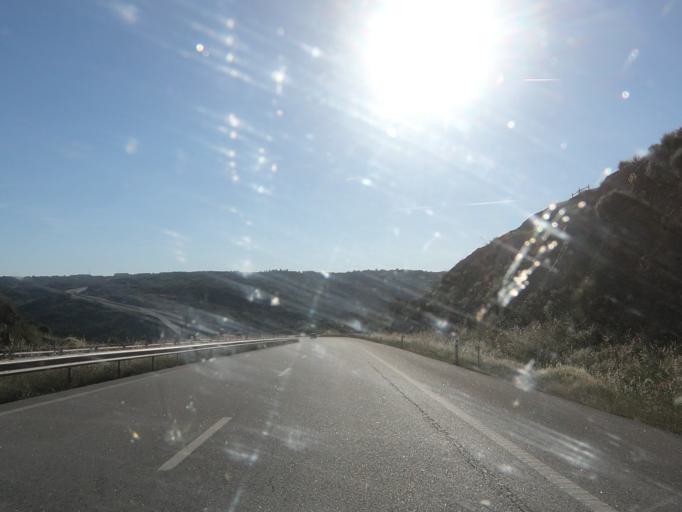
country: ES
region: Castille and Leon
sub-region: Provincia de Salamanca
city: Fuentes de Onoro
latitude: 40.6113
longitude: -6.9090
